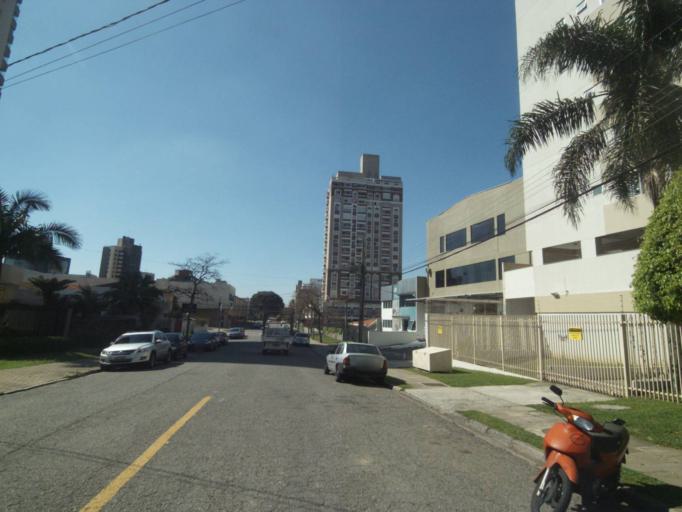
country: BR
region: Parana
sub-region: Curitiba
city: Curitiba
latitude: -25.4022
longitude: -49.2498
